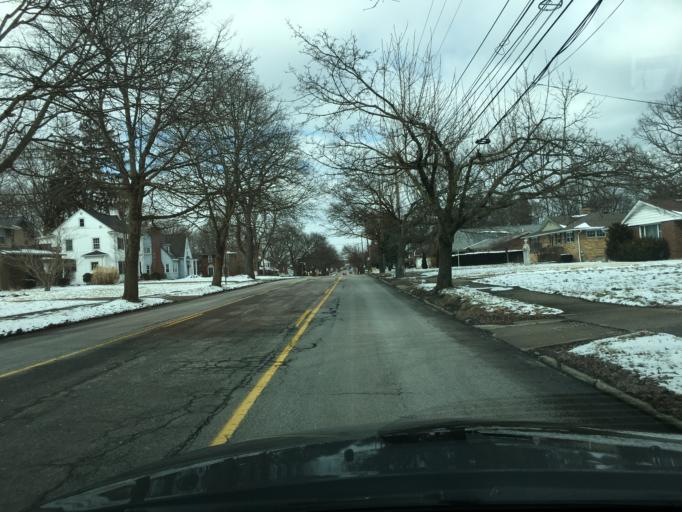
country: US
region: Ohio
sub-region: Summit County
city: Akron
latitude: 41.1052
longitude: -81.5638
